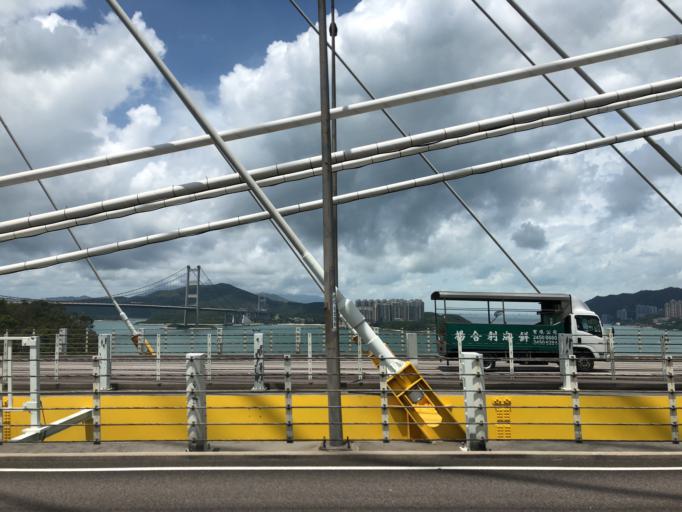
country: HK
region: Tsuen Wan
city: Tsuen Wan
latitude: 22.3613
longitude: 114.0813
